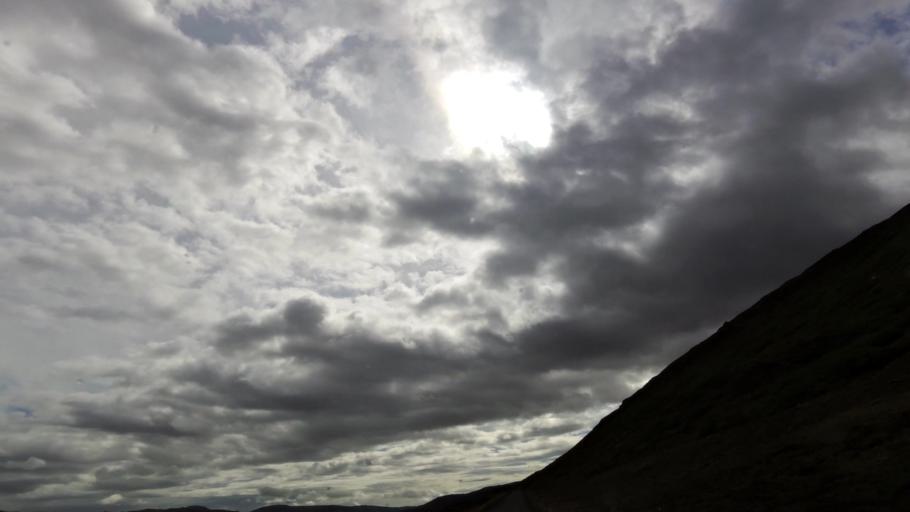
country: IS
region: West
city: Stykkisholmur
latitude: 65.5989
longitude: -22.1165
